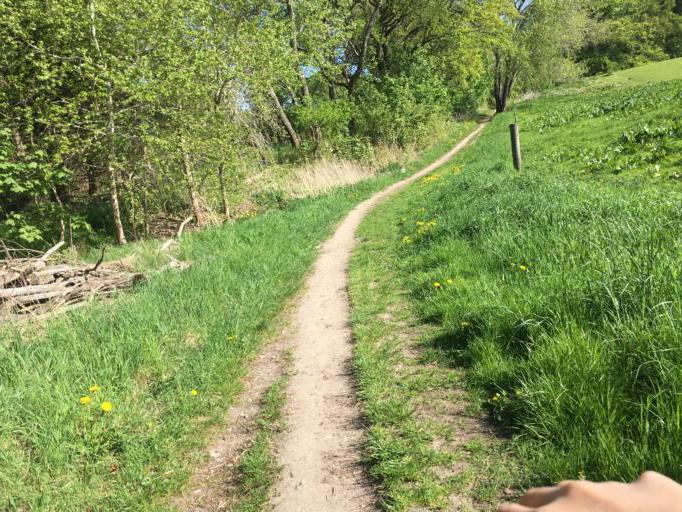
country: DK
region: Capital Region
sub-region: Ballerup Kommune
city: Ballerup
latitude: 55.7526
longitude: 12.3654
